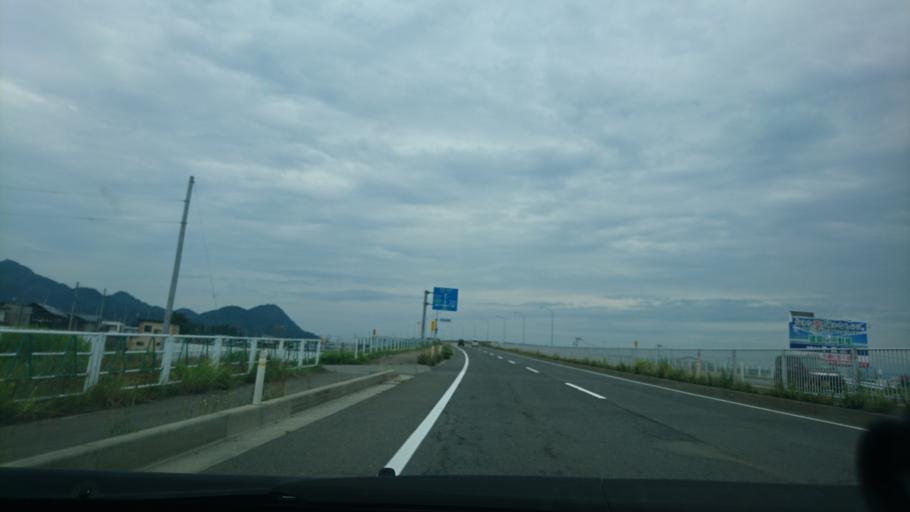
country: JP
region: Akita
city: Omagari
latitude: 39.4730
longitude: 140.4817
